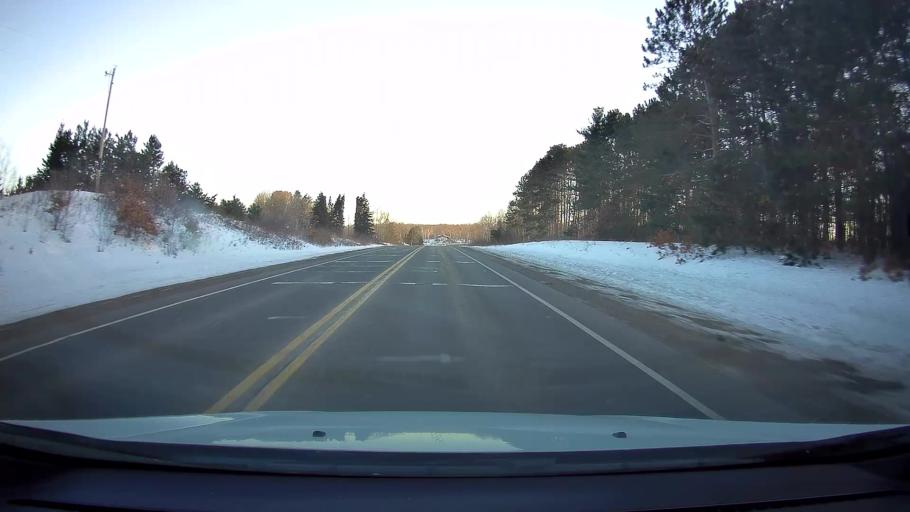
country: US
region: Wisconsin
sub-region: Barron County
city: Turtle Lake
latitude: 45.4050
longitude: -92.1397
